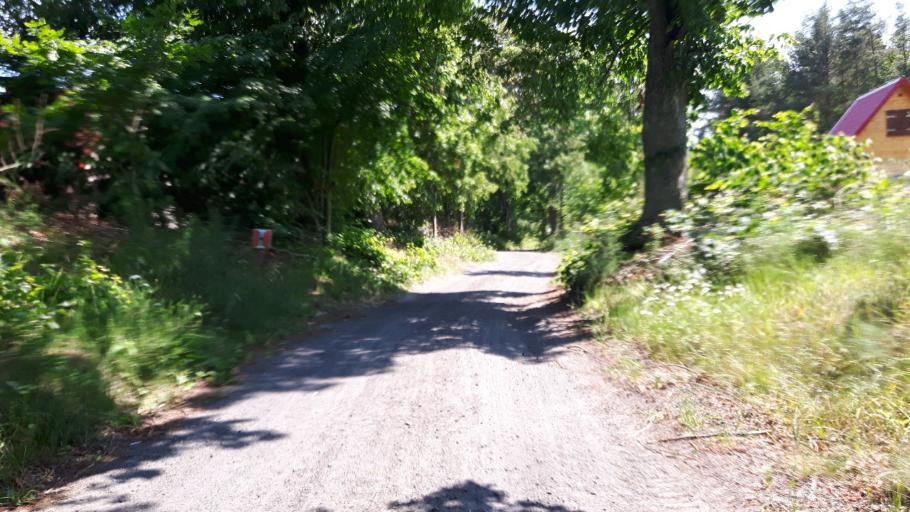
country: PL
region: Pomeranian Voivodeship
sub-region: Powiat wejherowski
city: Choczewo
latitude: 54.7326
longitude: 17.9531
